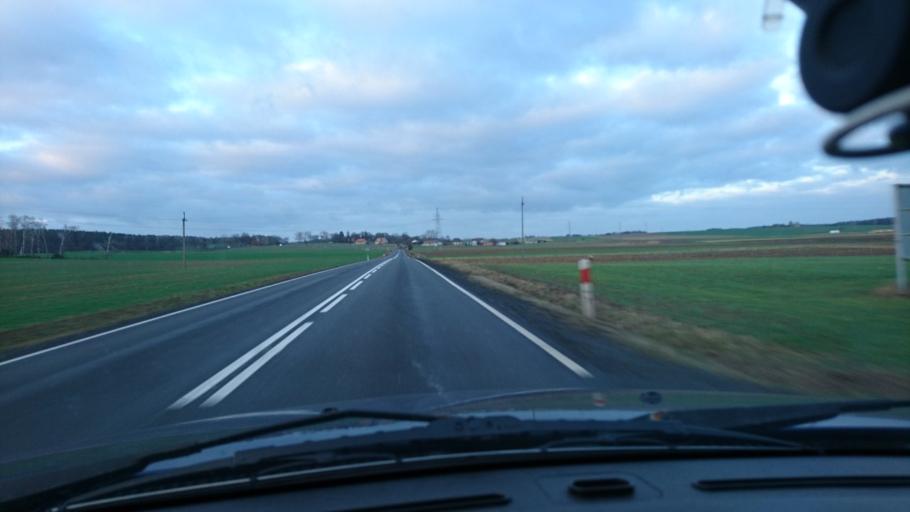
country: PL
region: Greater Poland Voivodeship
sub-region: Powiat ostrzeszowski
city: Ostrzeszow
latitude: 51.3603
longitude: 17.9465
